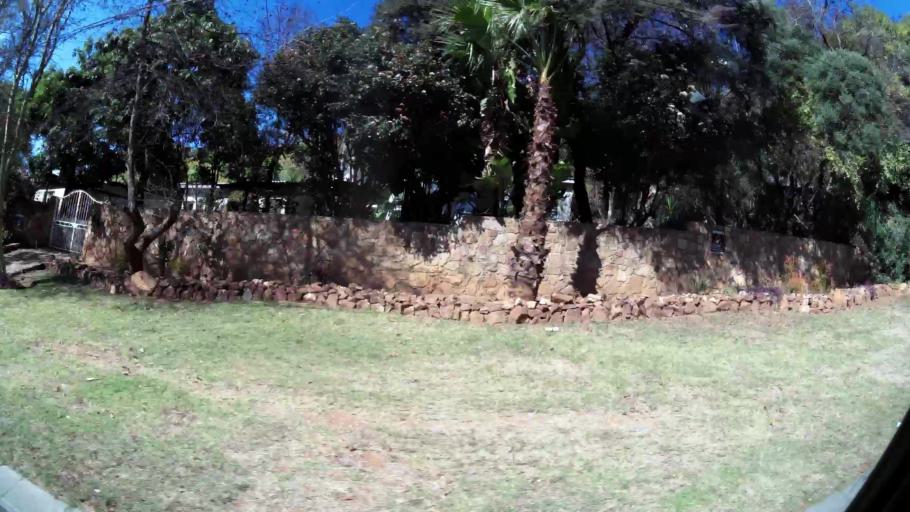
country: ZA
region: Gauteng
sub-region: City of Johannesburg Metropolitan Municipality
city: Roodepoort
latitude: -26.1399
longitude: 27.9048
